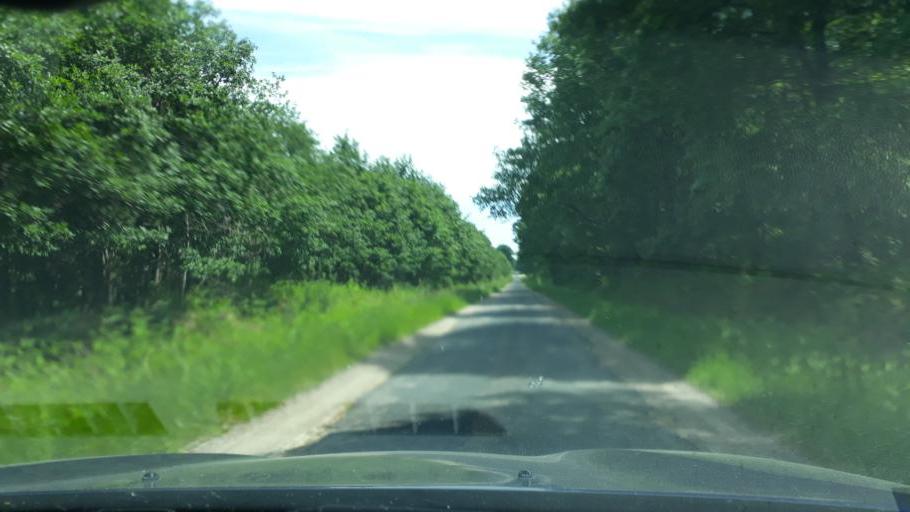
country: FR
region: Centre
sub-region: Departement du Loiret
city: Vitry-aux-Loges
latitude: 48.0240
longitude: 2.2881
